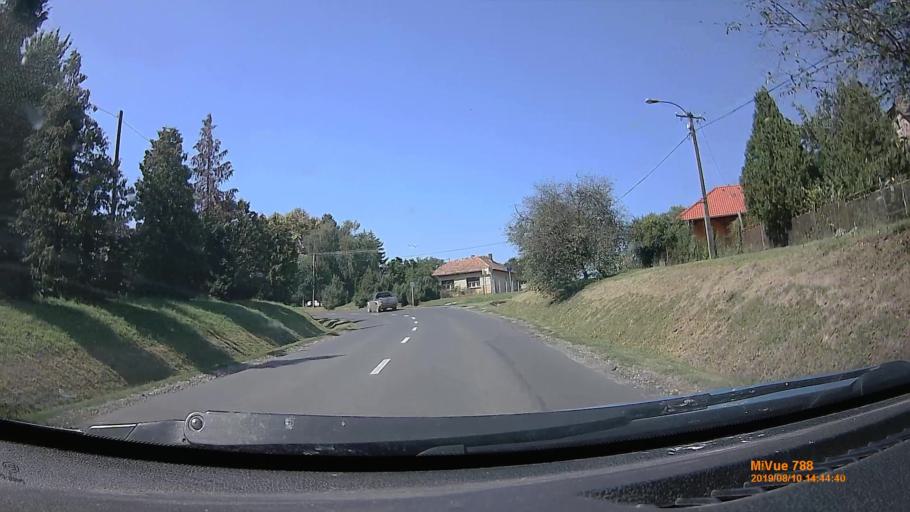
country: HU
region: Somogy
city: Somogyvar
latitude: 46.5810
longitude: 17.6486
